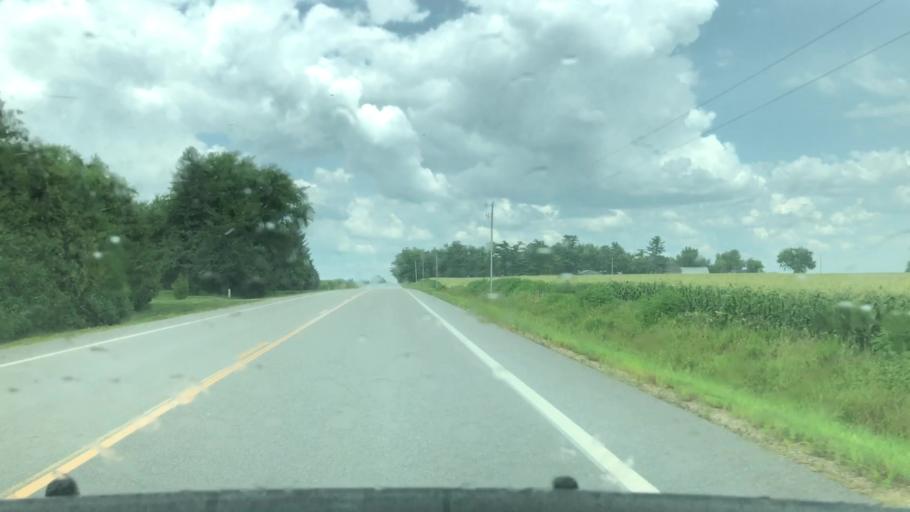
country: US
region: Minnesota
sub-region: Olmsted County
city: Stewartville
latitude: 43.8813
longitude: -92.5285
